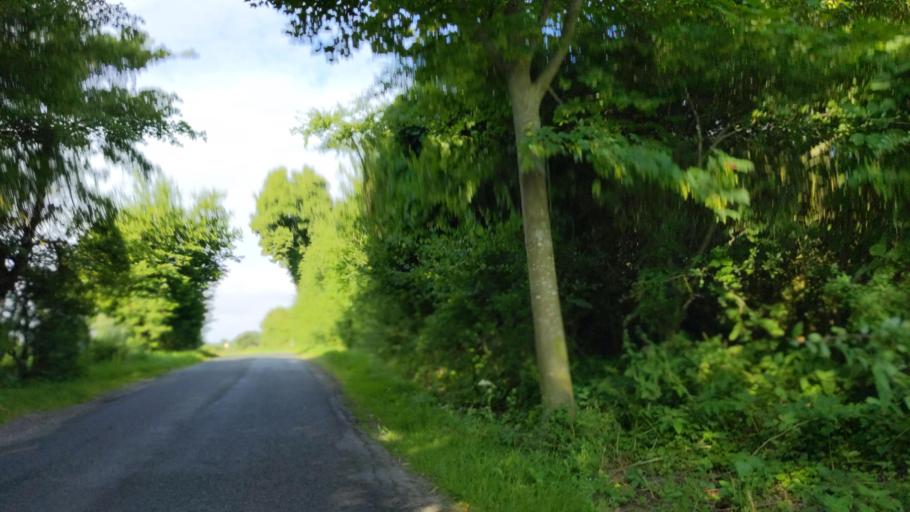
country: DE
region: Schleswig-Holstein
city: Bad Schwartau
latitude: 53.9687
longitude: 10.6661
